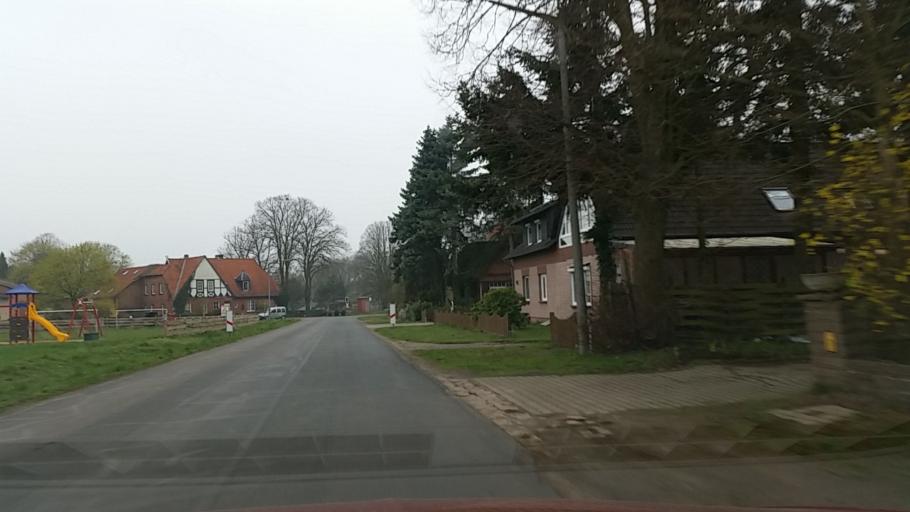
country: DE
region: Lower Saxony
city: Dedelstorf
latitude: 52.7048
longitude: 10.5363
